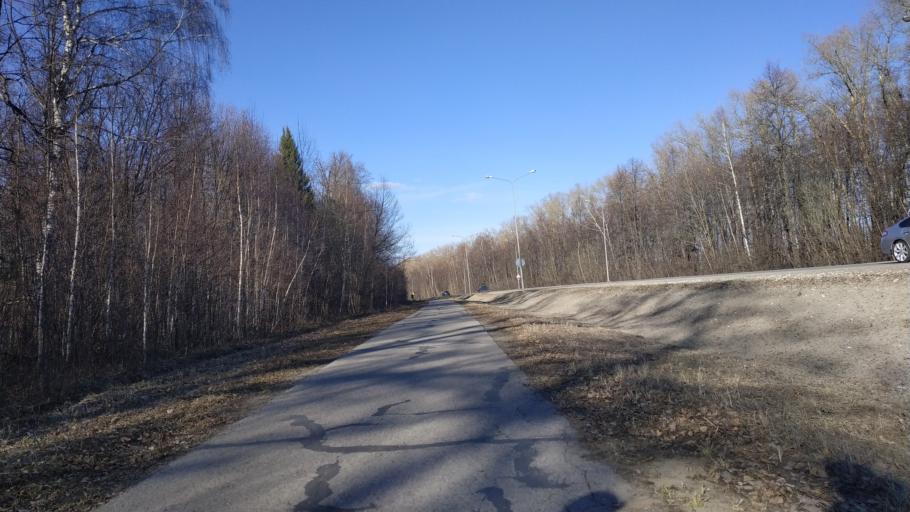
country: RU
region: Chuvashia
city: Ishley
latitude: 56.1278
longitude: 47.0682
